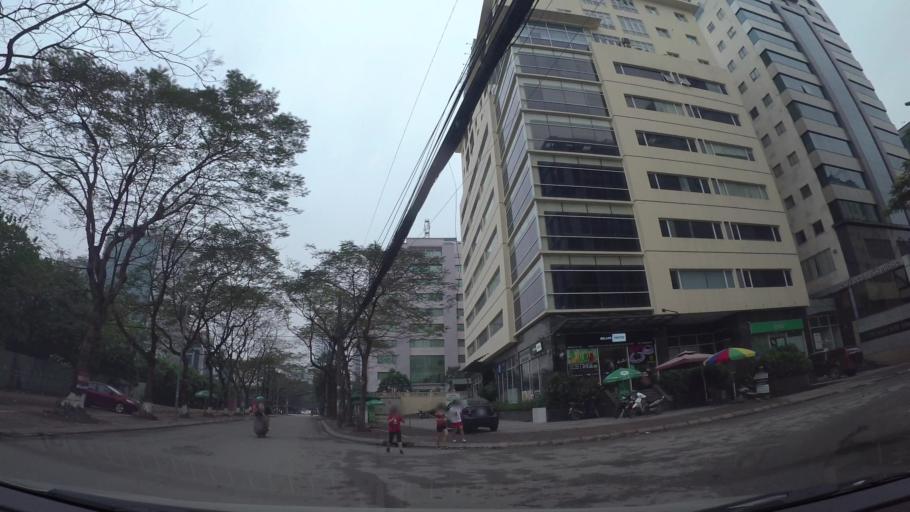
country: VN
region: Ha Noi
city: Cau Giay
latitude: 21.0323
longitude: 105.7834
